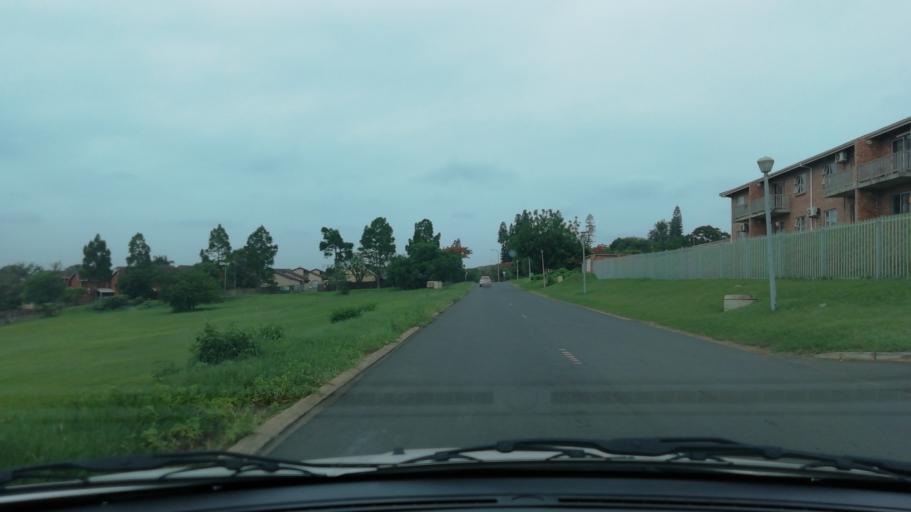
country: ZA
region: KwaZulu-Natal
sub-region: uThungulu District Municipality
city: Empangeni
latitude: -28.7414
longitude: 31.8865
